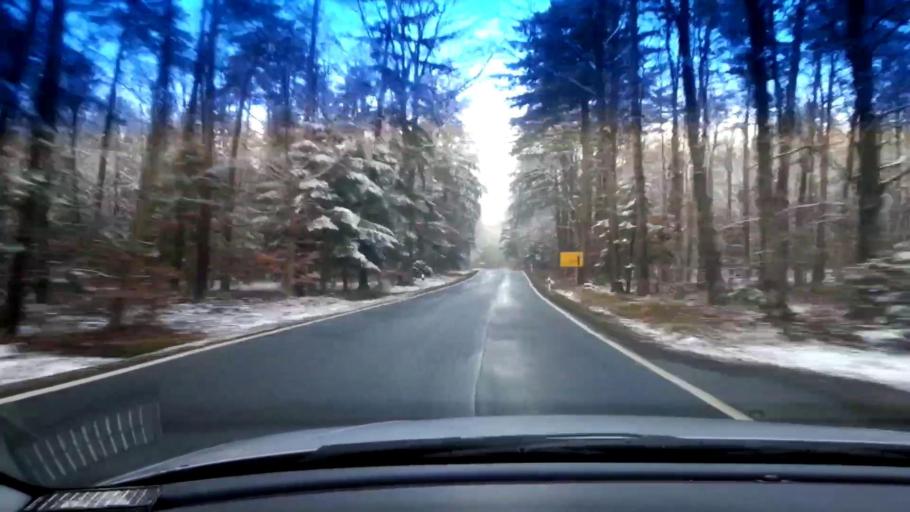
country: DE
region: Bavaria
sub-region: Upper Franconia
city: Pommersfelden
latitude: 49.7464
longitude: 10.8563
